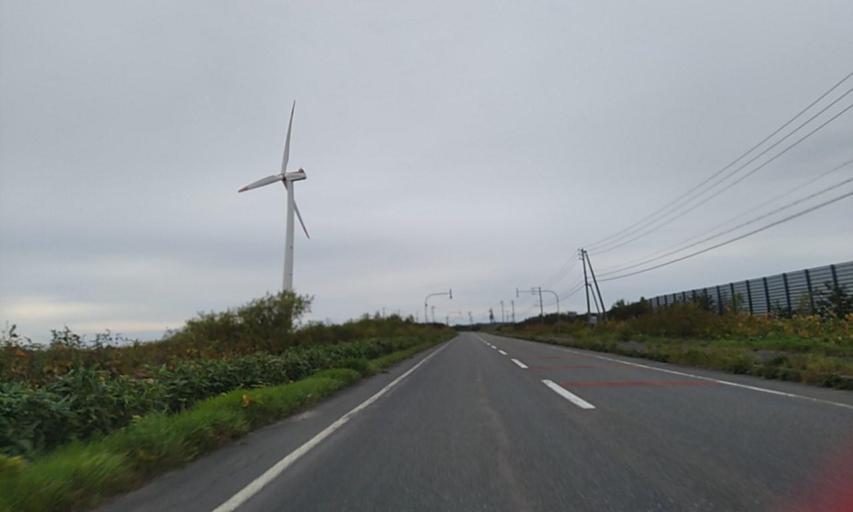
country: JP
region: Hokkaido
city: Makubetsu
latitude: 45.2848
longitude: 142.2186
